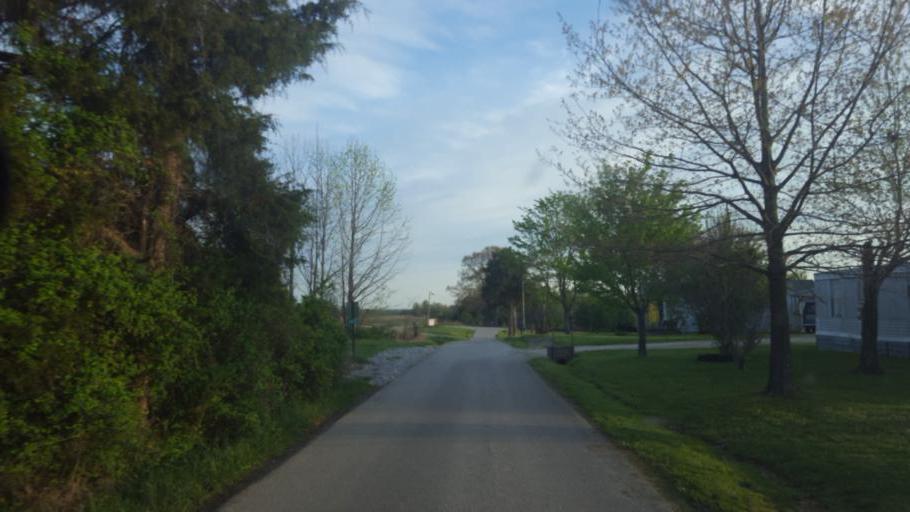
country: US
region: Kentucky
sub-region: Barren County
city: Cave City
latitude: 37.1607
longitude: -86.0126
